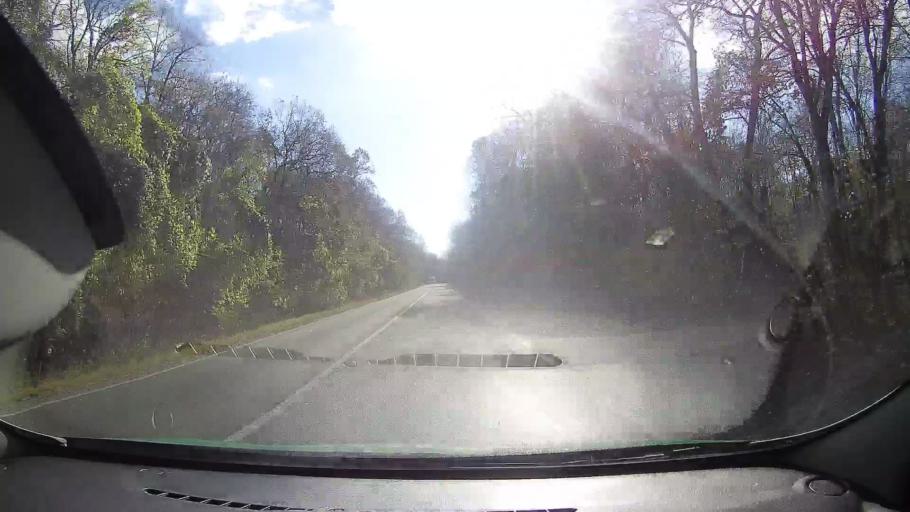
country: RO
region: Tulcea
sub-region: Oras Babadag
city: Babadag
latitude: 44.8478
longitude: 28.6988
